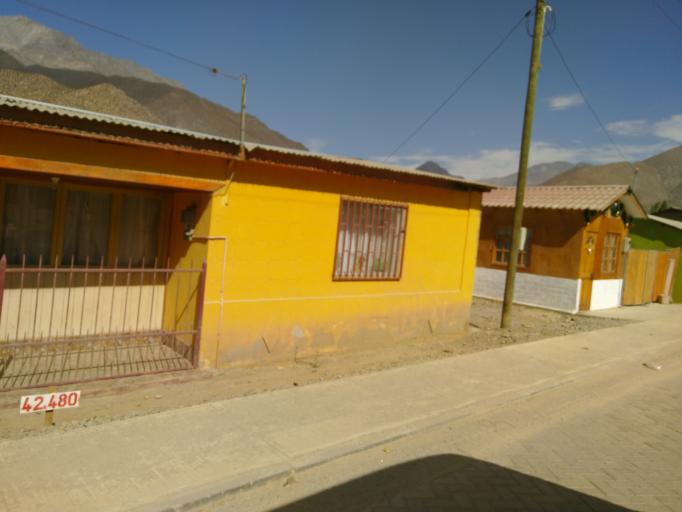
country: CL
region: Coquimbo
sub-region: Provincia de Limari
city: Monte Patria
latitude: -30.9588
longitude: -70.7726
